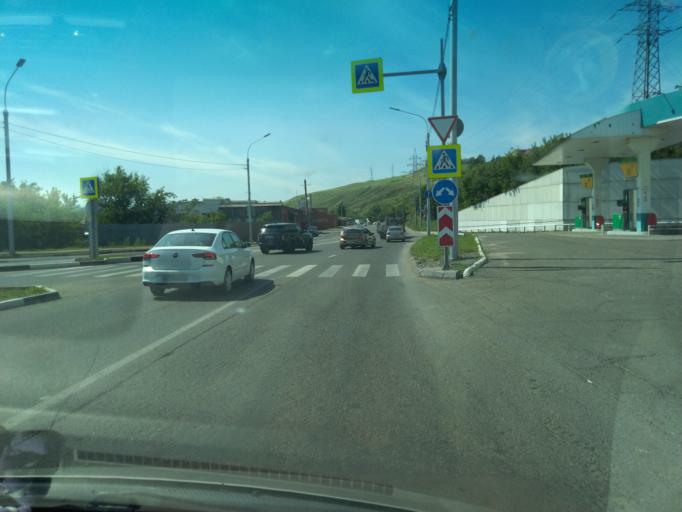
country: RU
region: Krasnoyarskiy
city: Krasnoyarsk
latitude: 56.0200
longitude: 92.8755
